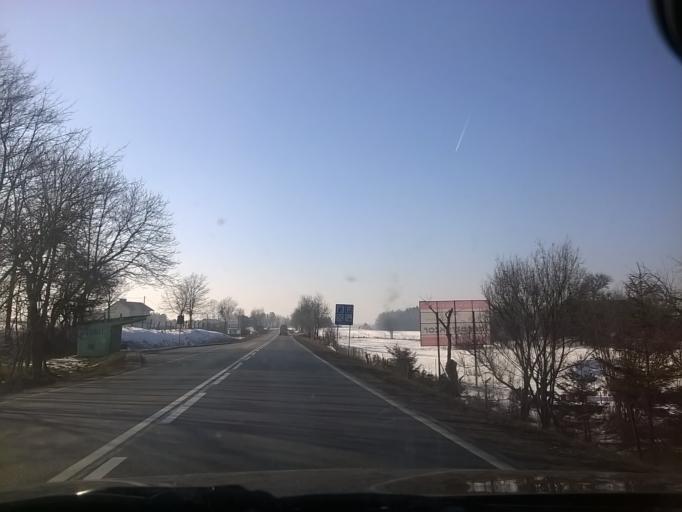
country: PL
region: Warmian-Masurian Voivodeship
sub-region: Powiat mragowski
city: Mragowo
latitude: 53.8466
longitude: 21.2282
